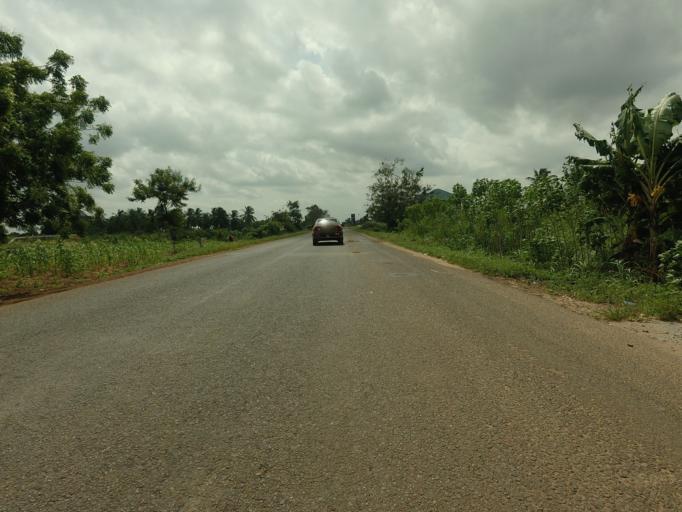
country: TG
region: Maritime
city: Lome
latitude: 6.1345
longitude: 1.1179
